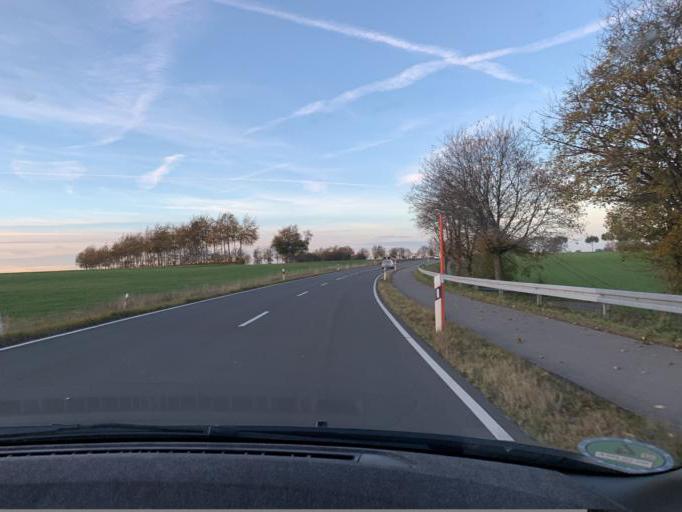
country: DE
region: North Rhine-Westphalia
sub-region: Regierungsbezirk Koln
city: Simmerath
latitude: 50.6137
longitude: 6.3290
